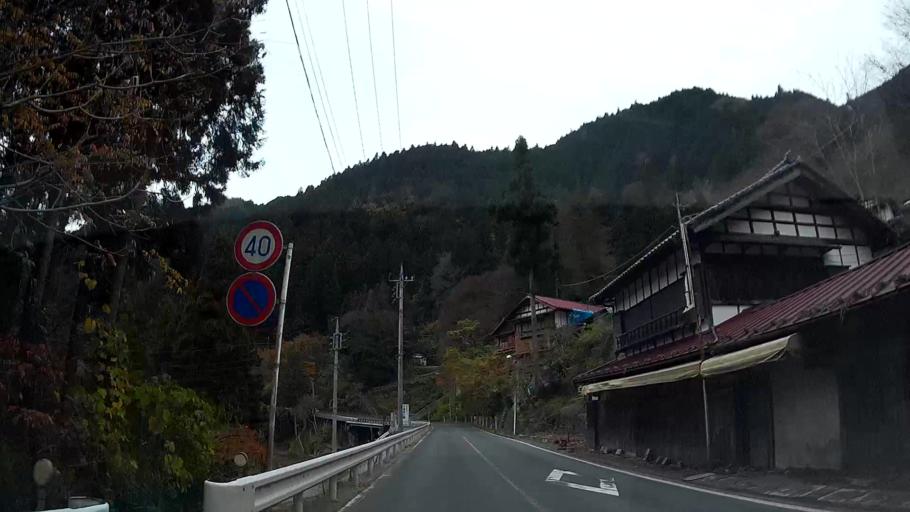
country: JP
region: Saitama
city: Chichibu
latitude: 35.9522
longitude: 138.9631
